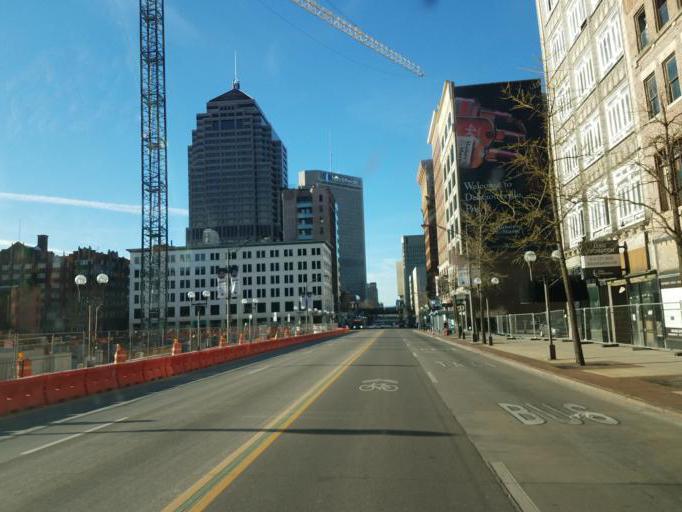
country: US
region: Ohio
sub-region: Franklin County
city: Columbus
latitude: 39.9636
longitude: -83.0010
